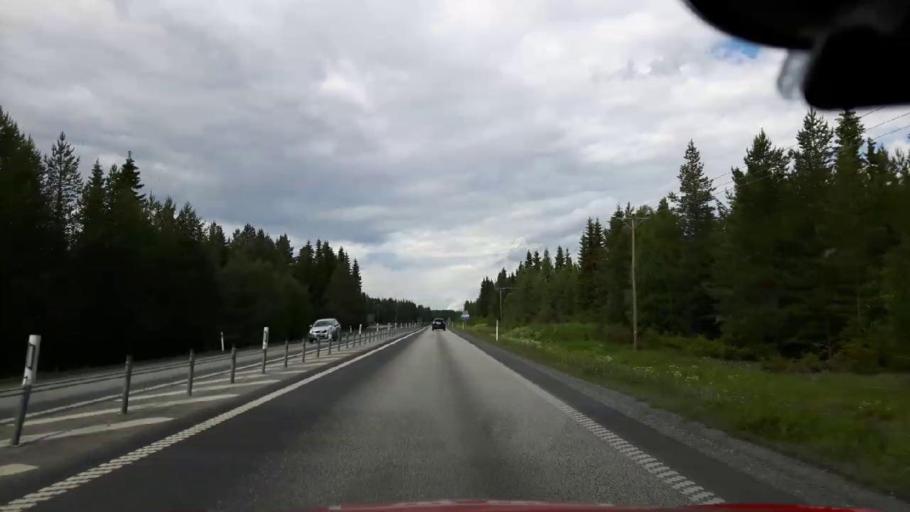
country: SE
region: Jaemtland
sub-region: OEstersunds Kommun
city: Ostersund
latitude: 63.2270
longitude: 14.6193
